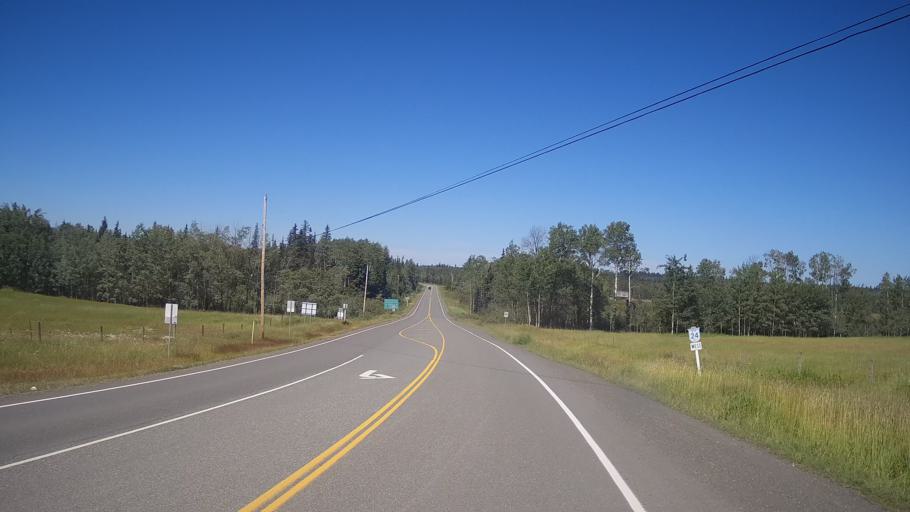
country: CA
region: British Columbia
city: Cache Creek
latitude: 51.5471
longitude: -120.9163
